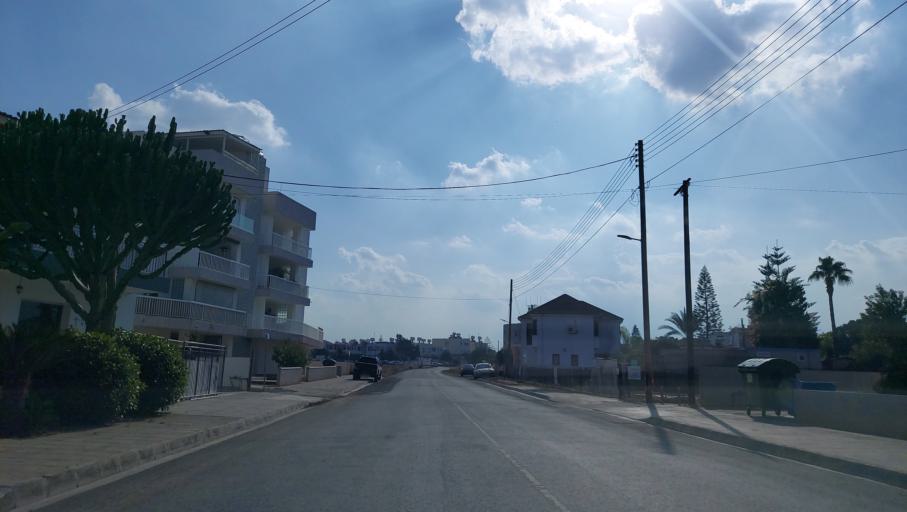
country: CY
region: Lefkosia
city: Tseri
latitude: 35.1033
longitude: 33.3074
